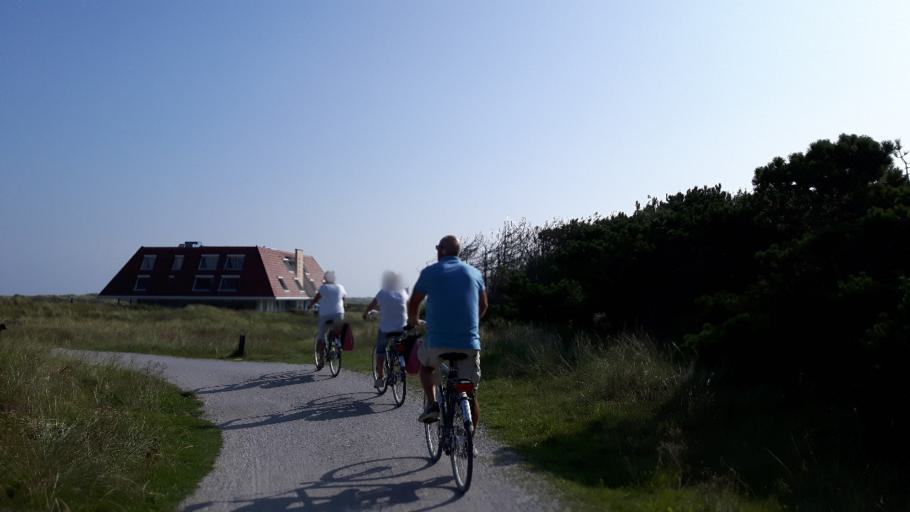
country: NL
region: Friesland
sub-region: Gemeente Ameland
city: Nes
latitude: 53.4595
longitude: 5.8054
